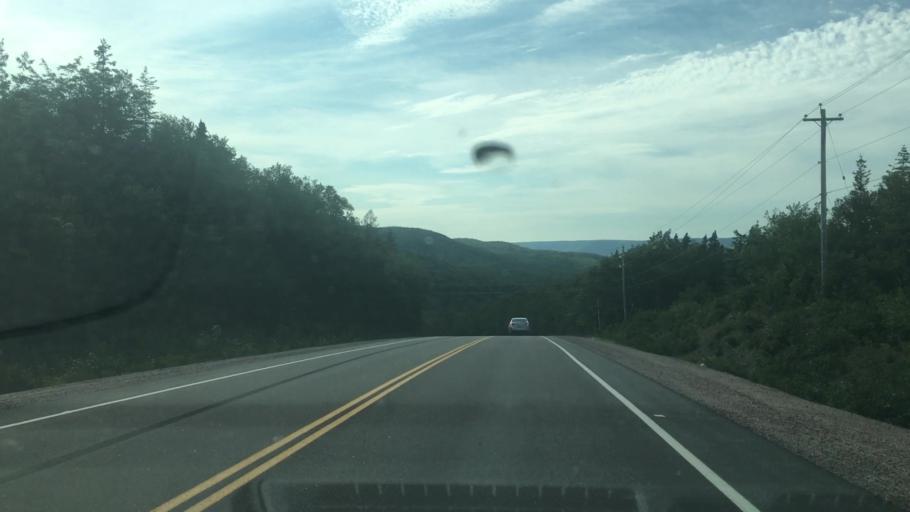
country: CA
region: Nova Scotia
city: Sydney Mines
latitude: 46.8554
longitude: -60.4480
